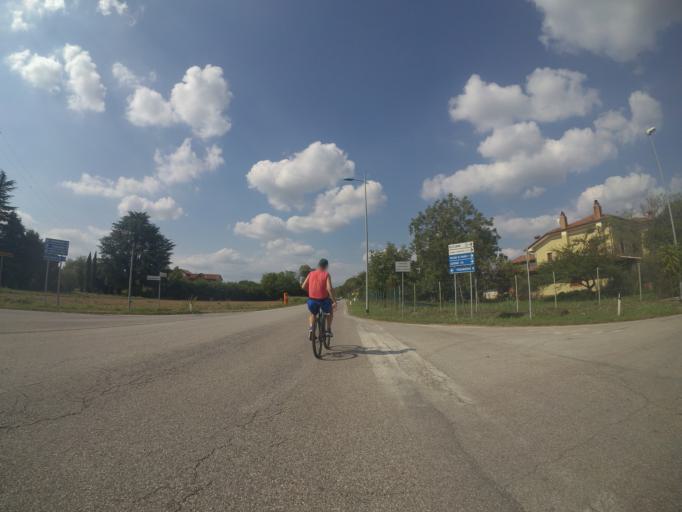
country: IT
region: Friuli Venezia Giulia
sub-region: Provincia di Udine
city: Basiliano-Vissandone
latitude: 46.0403
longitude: 13.0994
